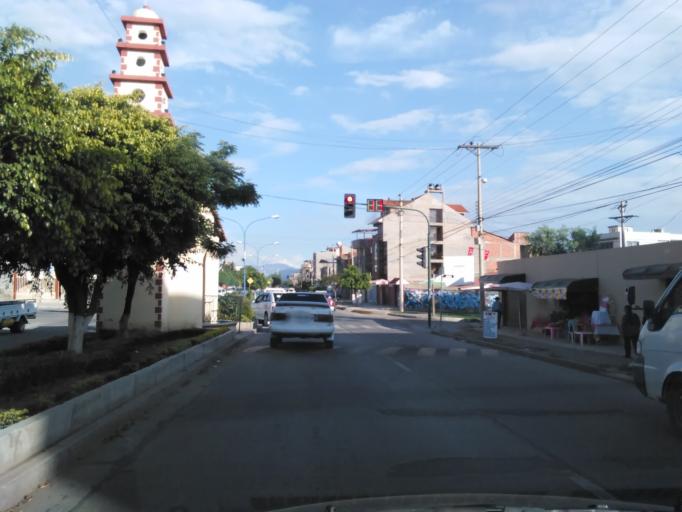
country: BO
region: Cochabamba
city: Cochabamba
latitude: -17.3526
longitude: -66.1902
